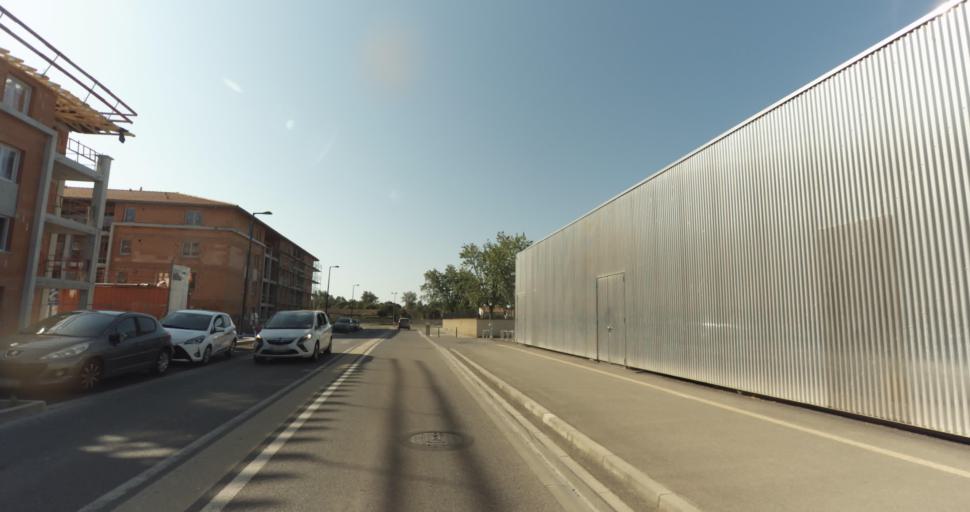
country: FR
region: Midi-Pyrenees
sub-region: Departement de la Haute-Garonne
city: Plaisance-du-Touch
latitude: 43.5623
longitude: 1.2922
